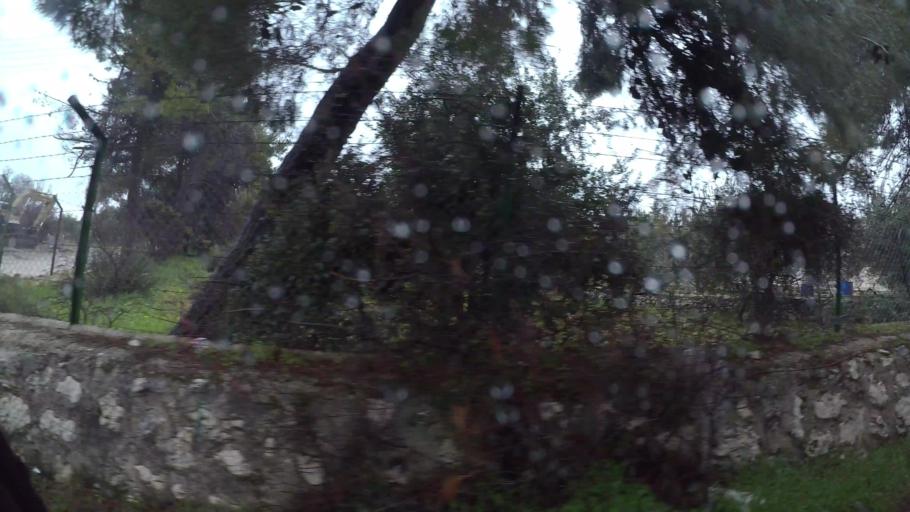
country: JO
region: Amman
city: Wadi as Sir
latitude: 32.0059
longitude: 35.7982
